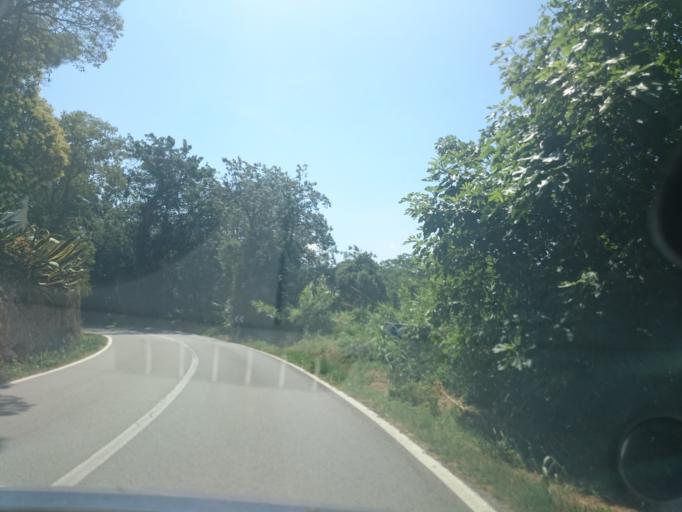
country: ES
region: Catalonia
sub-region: Provincia de Barcelona
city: Sant Pere de Riudebitlles
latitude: 41.4584
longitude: 1.6738
